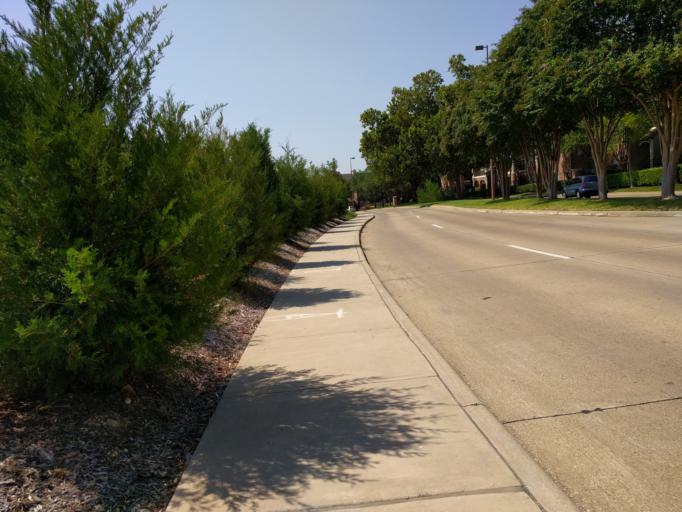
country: US
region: Texas
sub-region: Dallas County
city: Richardson
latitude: 32.9183
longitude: -96.7736
